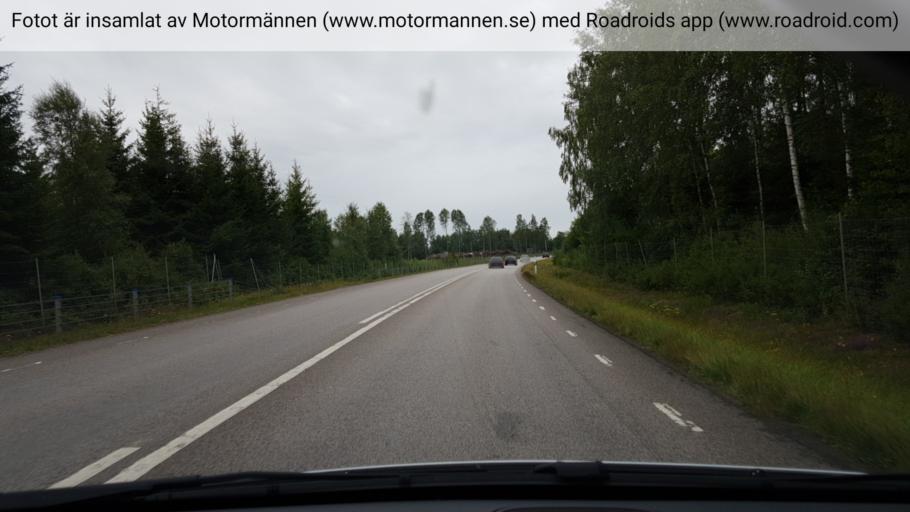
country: SE
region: Vaestra Goetaland
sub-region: Tibro Kommun
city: Tibro
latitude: 58.4357
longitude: 14.1733
